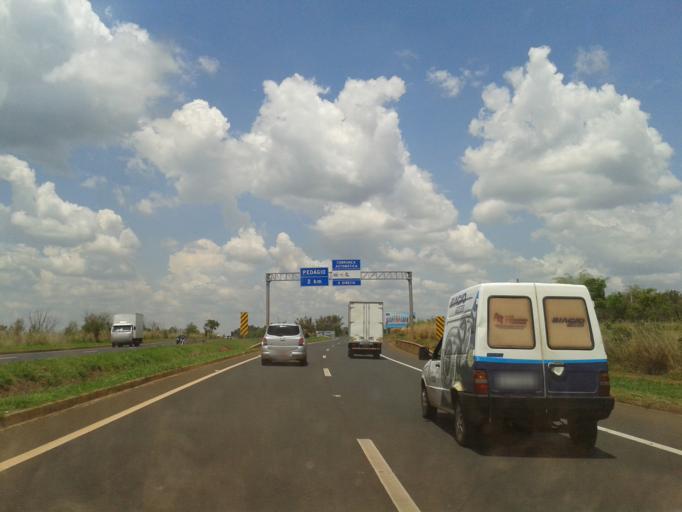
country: BR
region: Minas Gerais
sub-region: Araguari
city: Araguari
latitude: -18.7338
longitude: -48.2253
